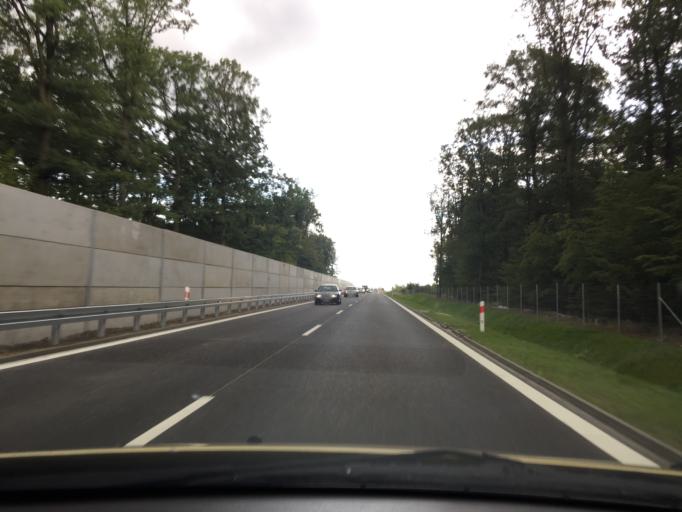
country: PL
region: Greater Poland Voivodeship
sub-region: Powiat jarocinski
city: Jarocin
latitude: 51.9632
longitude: 17.5229
